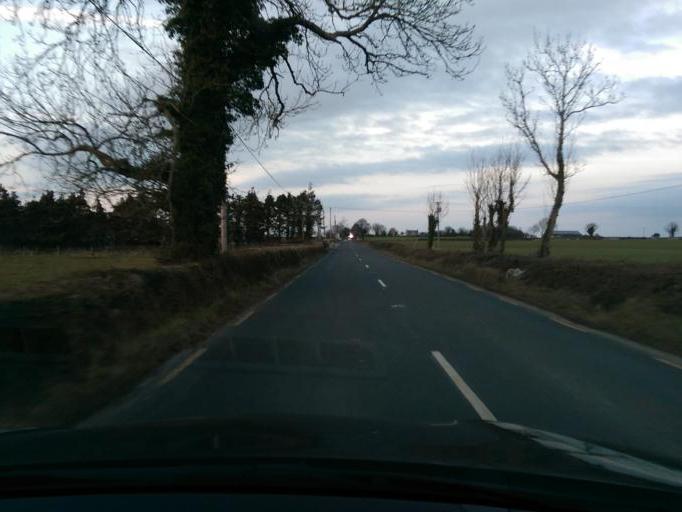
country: IE
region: Connaught
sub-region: County Galway
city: Portumna
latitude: 53.0430
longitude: -8.1124
